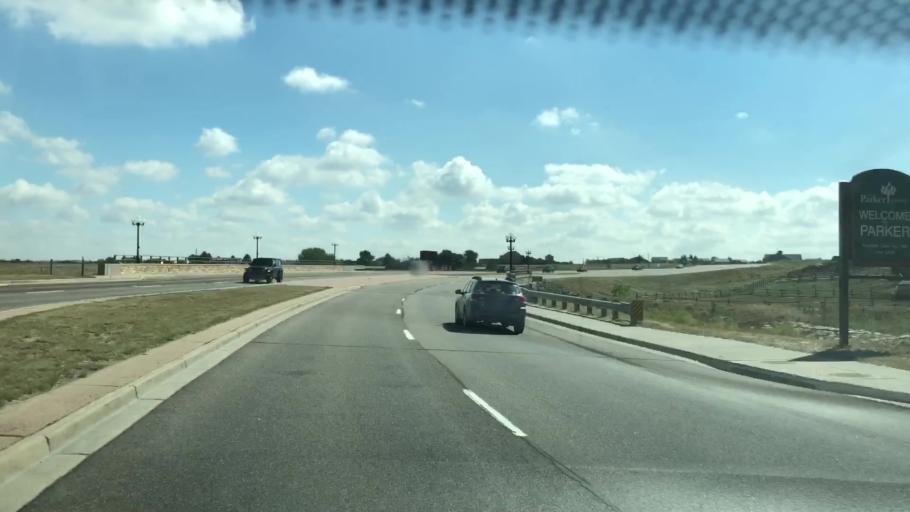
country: US
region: Colorado
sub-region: Douglas County
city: Stonegate
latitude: 39.5172
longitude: -104.8120
